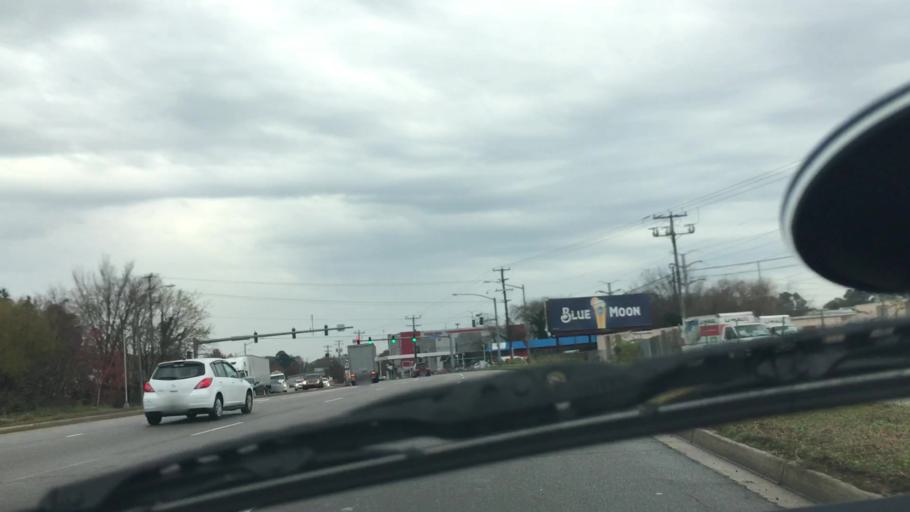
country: US
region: Virginia
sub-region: City of Norfolk
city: Norfolk
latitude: 36.9026
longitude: -76.2567
